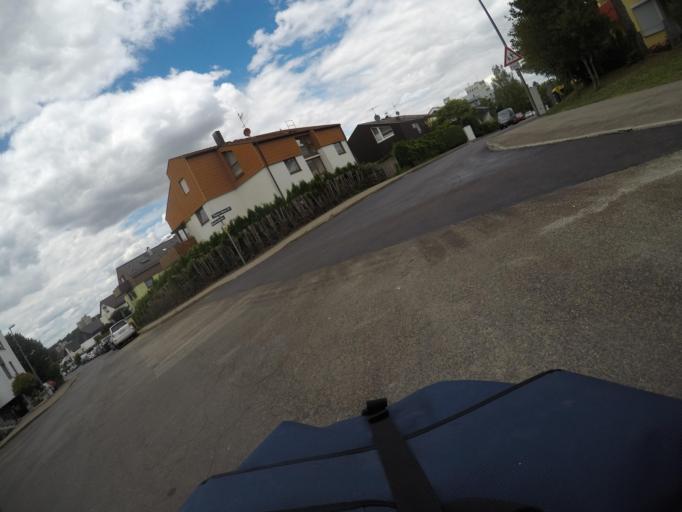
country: DE
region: Baden-Wuerttemberg
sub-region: Regierungsbezirk Stuttgart
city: Stuttgart Feuerbach
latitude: 48.8060
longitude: 9.1456
